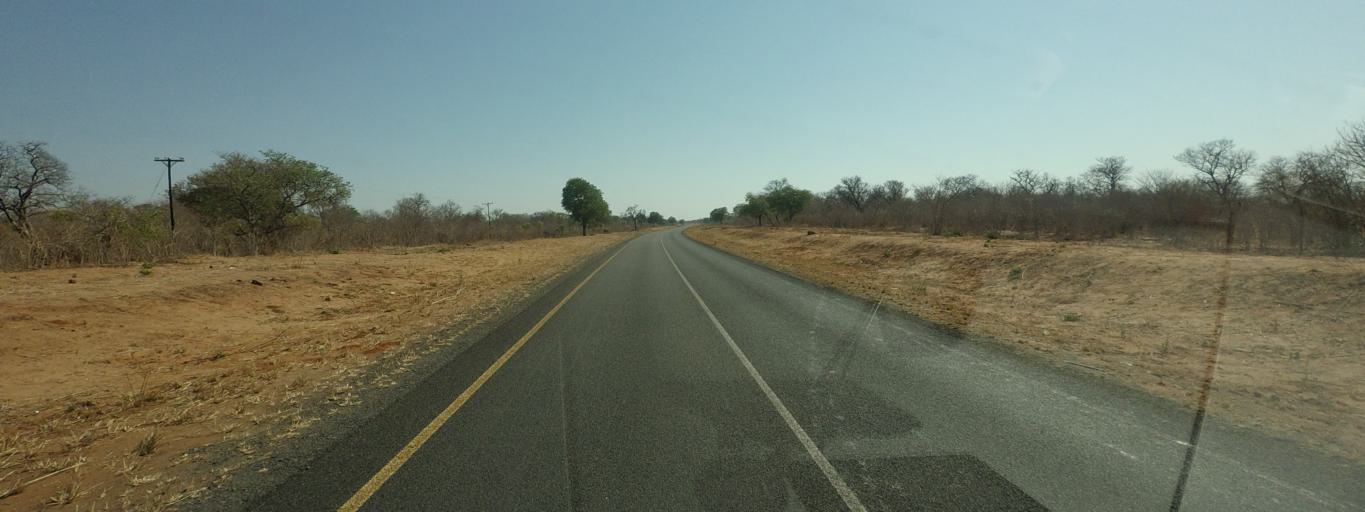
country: BW
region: North West
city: Kasane
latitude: -17.8645
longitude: 25.2212
